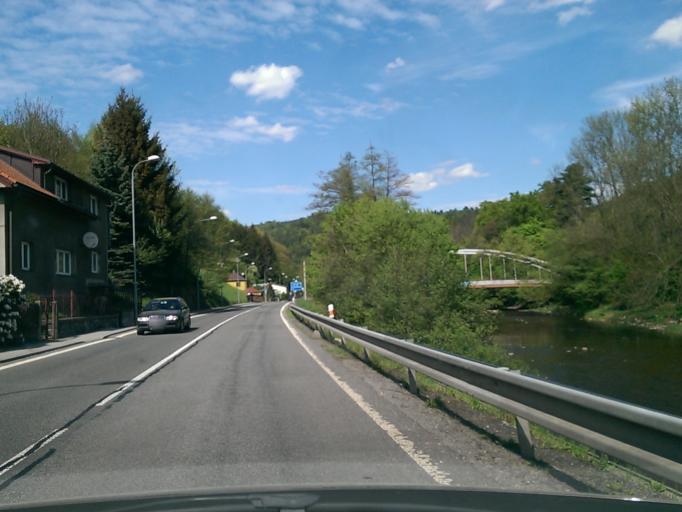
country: CZ
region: Liberecky
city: Mala Skala
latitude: 50.6477
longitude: 15.2093
